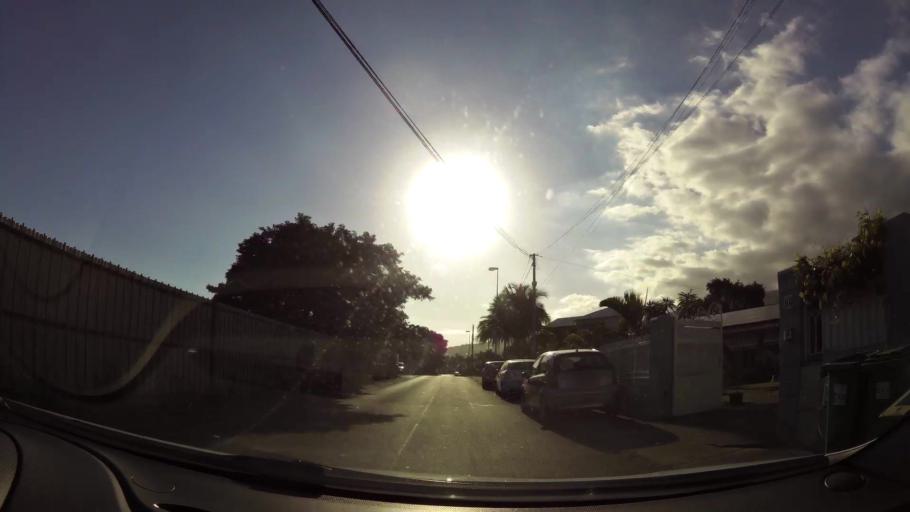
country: RE
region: Reunion
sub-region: Reunion
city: Les Avirons
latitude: -21.2665
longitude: 55.3646
